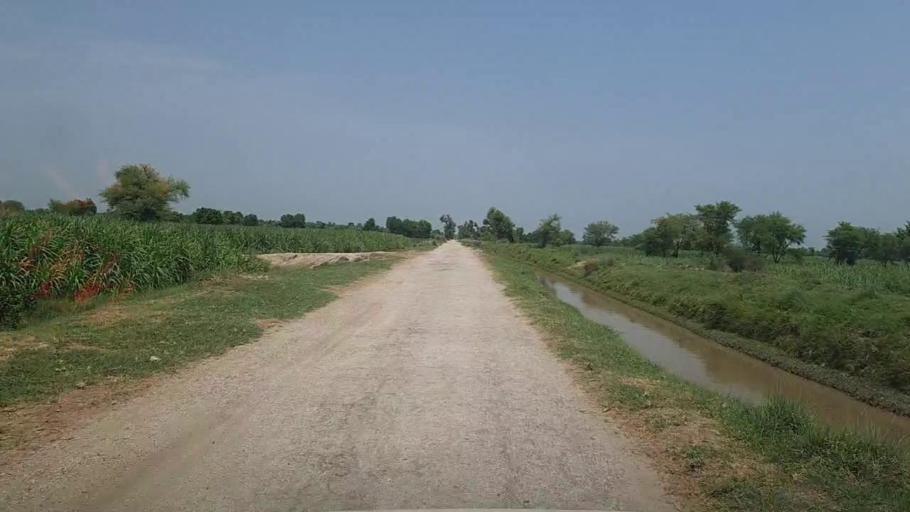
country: PK
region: Sindh
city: Karaundi
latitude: 26.8874
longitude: 68.3338
